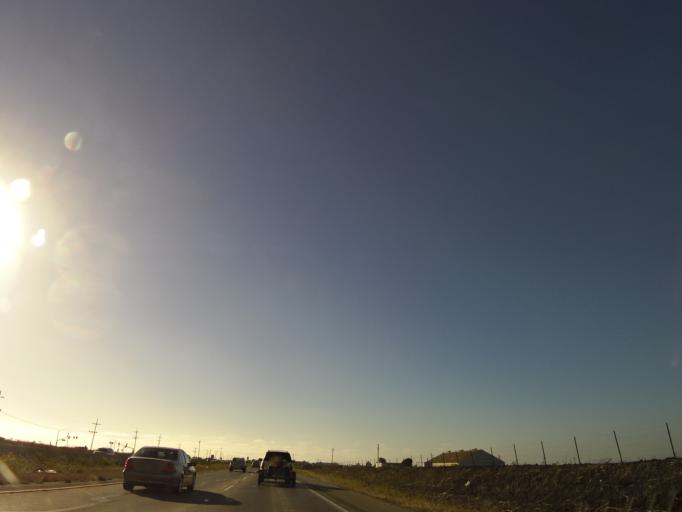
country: US
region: California
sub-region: Monterey County
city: Salinas
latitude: 36.6436
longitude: -121.6091
